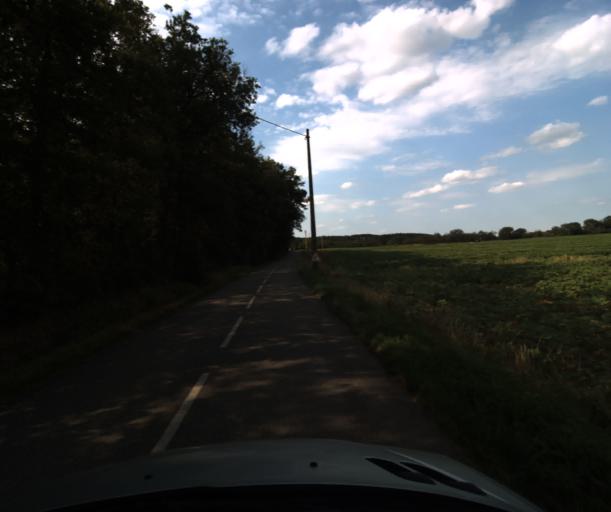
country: FR
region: Midi-Pyrenees
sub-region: Departement de la Haute-Garonne
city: Fonsorbes
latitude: 43.5133
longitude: 1.2213
